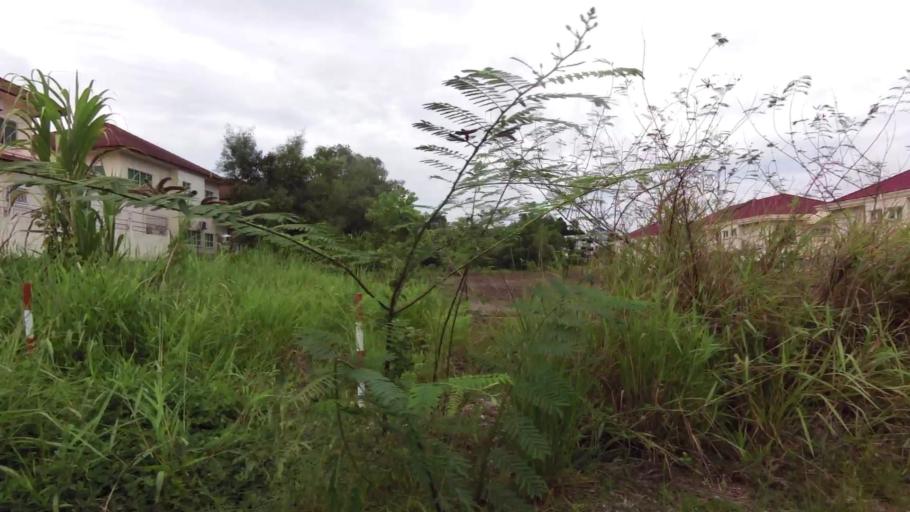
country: BN
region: Brunei and Muara
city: Bandar Seri Begawan
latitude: 4.8887
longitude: 114.9118
